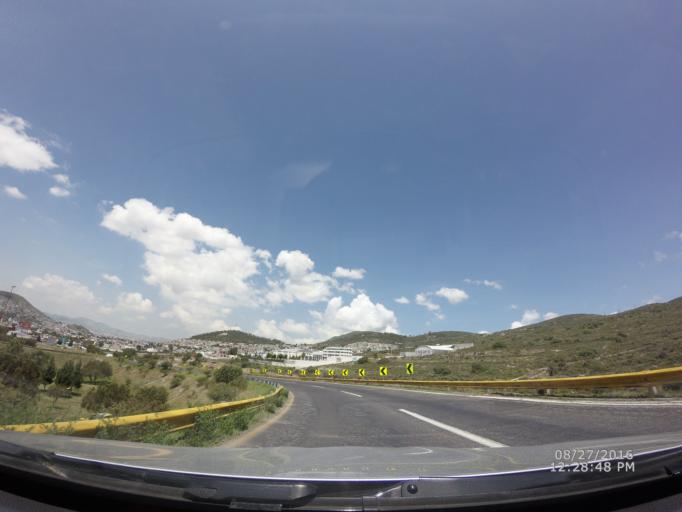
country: MX
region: Hidalgo
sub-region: Mineral de la Reforma
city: Rio de la Soledad
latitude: 20.1195
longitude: -98.7089
